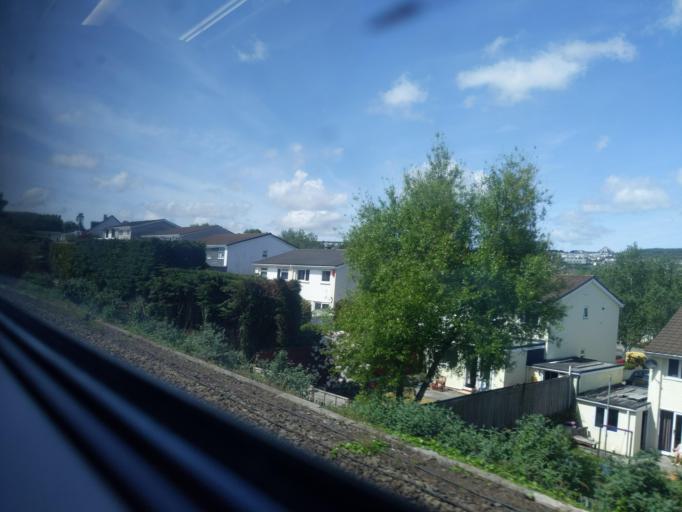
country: GB
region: England
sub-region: Cornwall
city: St Austell
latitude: 50.3392
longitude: -4.7693
